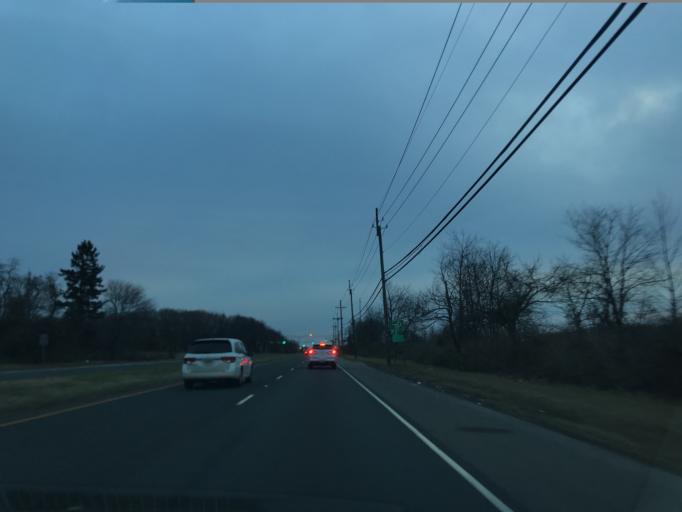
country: US
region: New Jersey
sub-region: Middlesex County
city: Dayton
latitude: 40.3535
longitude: -74.4960
